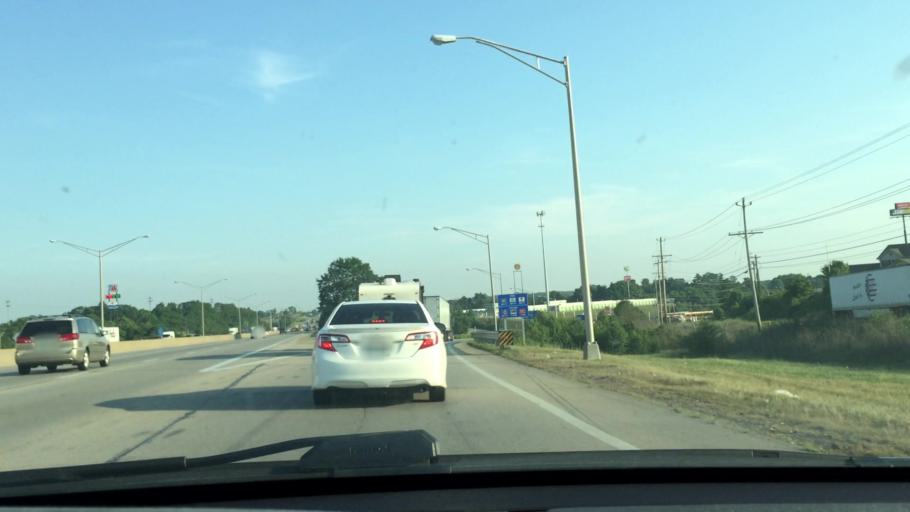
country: US
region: Kentucky
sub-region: Boone County
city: Walton
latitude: 38.9211
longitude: -84.6304
